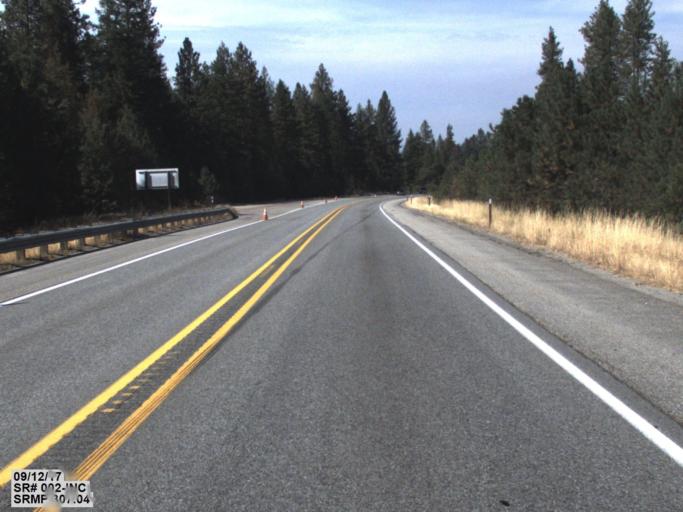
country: US
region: Washington
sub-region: Spokane County
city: Deer Park
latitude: 47.9262
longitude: -117.3508
